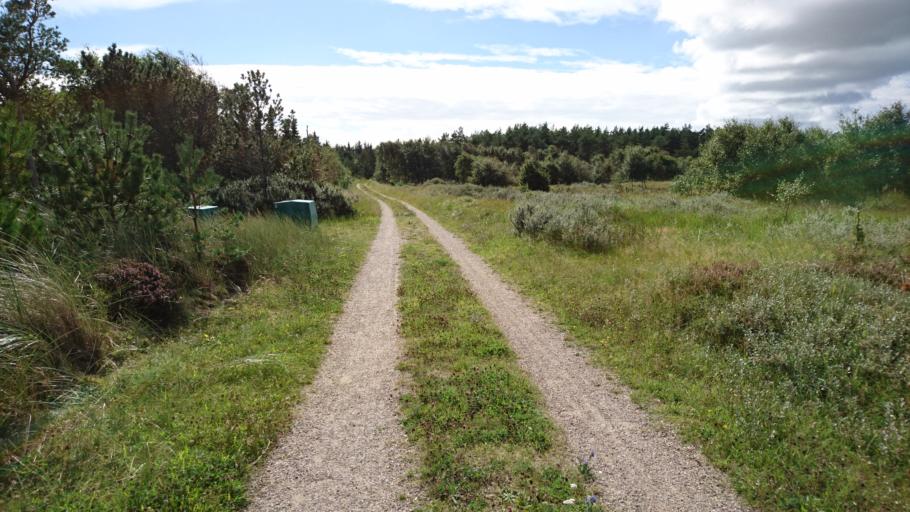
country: DK
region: North Denmark
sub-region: Frederikshavn Kommune
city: Skagen
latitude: 57.7132
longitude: 10.5139
